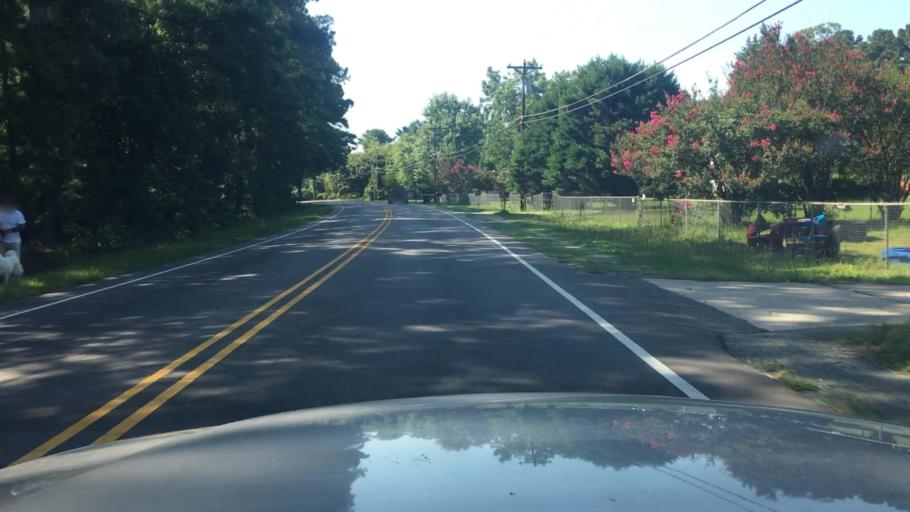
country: US
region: North Carolina
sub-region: Cumberland County
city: Fayetteville
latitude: 35.1063
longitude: -78.9017
